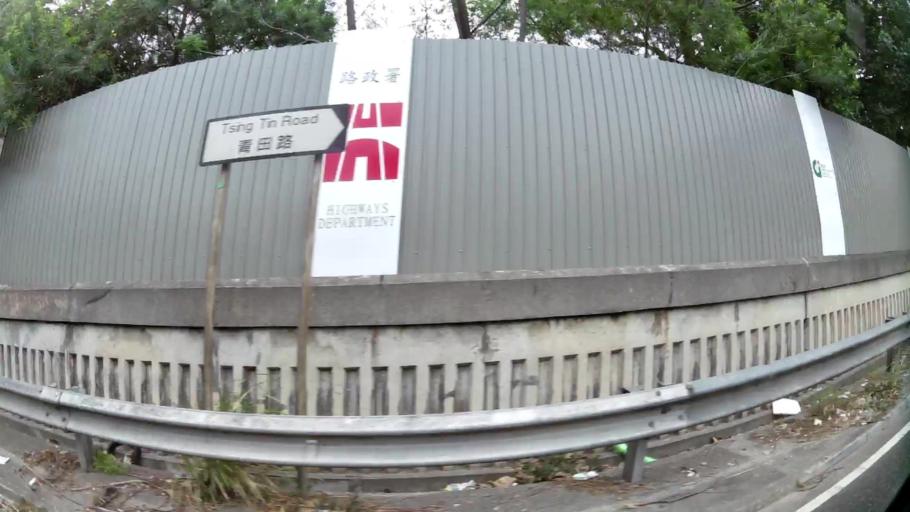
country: HK
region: Tuen Mun
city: Tuen Mun
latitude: 22.4060
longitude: 113.9783
